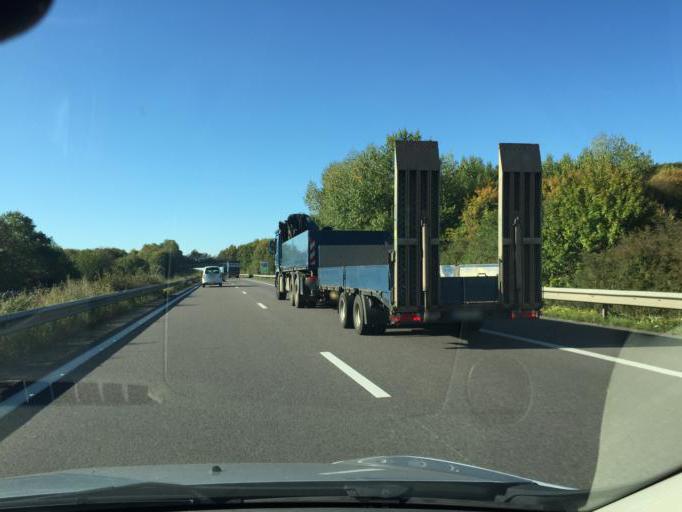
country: LU
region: Grevenmacher
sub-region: Canton de Grevenmacher
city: Flaxweiler
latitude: 49.6532
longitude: 6.3369
